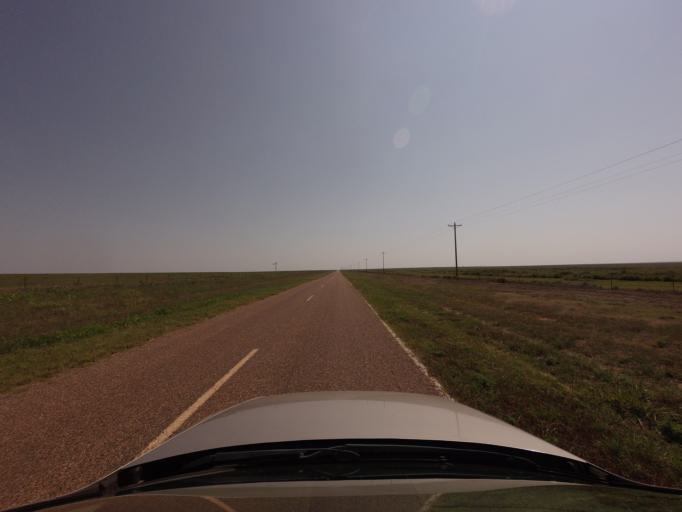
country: US
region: New Mexico
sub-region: Curry County
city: Cannon Air Force Base
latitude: 34.6330
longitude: -103.3853
